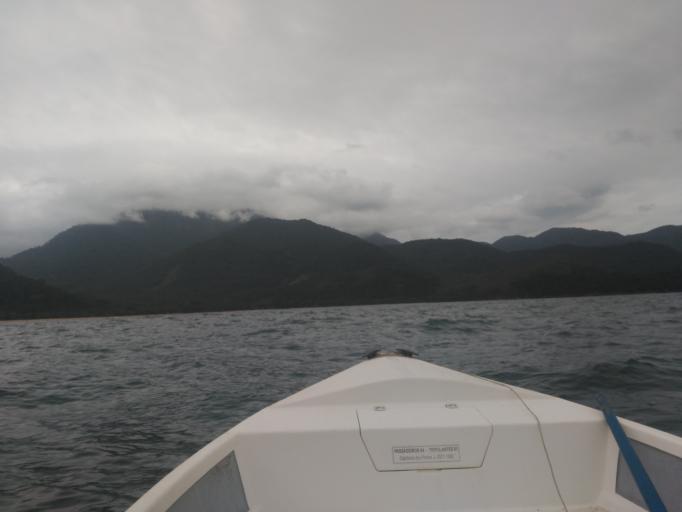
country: BR
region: Rio de Janeiro
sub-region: Parati
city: Paraty
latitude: -23.3408
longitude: -44.6443
